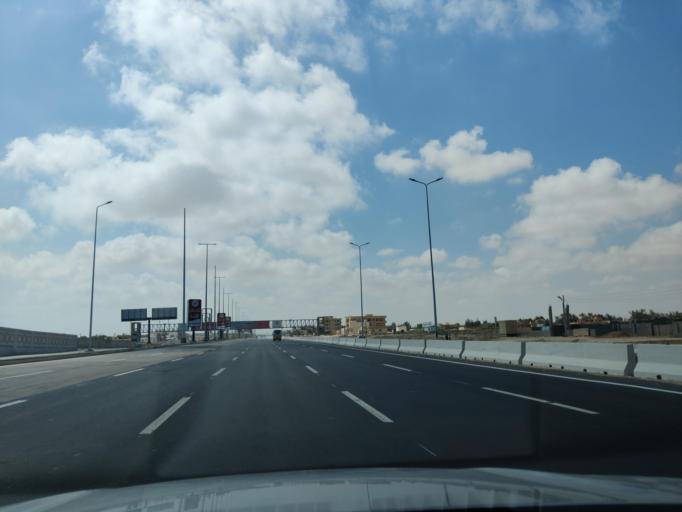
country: EG
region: Muhafazat Matruh
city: Al `Alamayn
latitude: 30.9498
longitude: 28.7730
